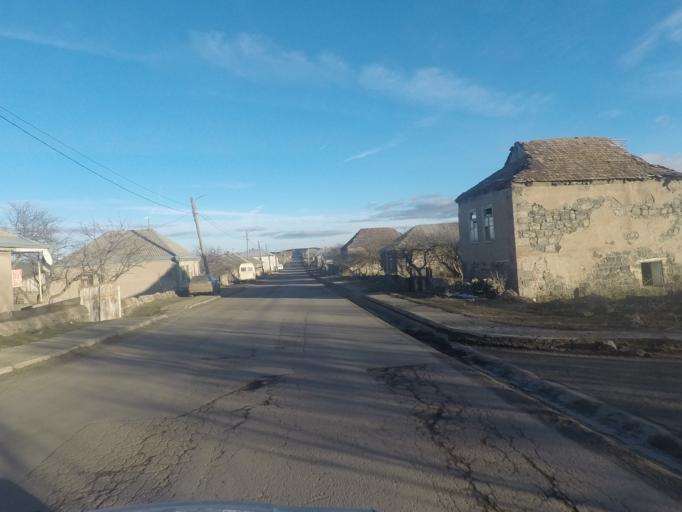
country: GE
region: Kvemo Kartli
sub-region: Tsalka
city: Tsalka
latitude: 41.6053
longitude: 44.0431
